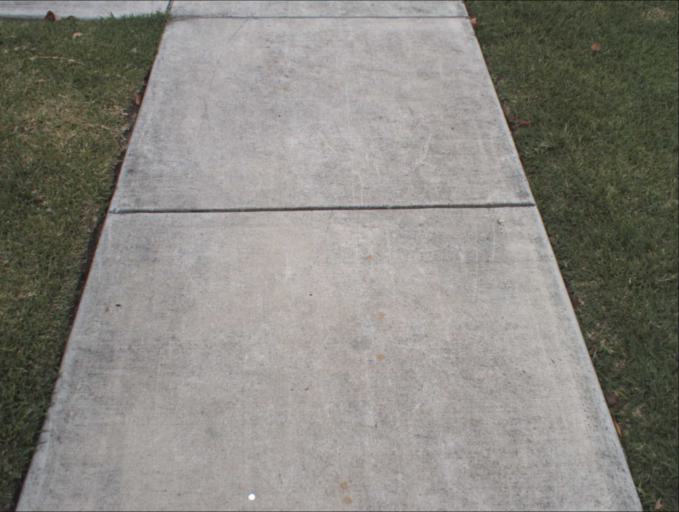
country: AU
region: Queensland
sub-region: Logan
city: Beenleigh
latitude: -27.7163
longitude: 153.1957
